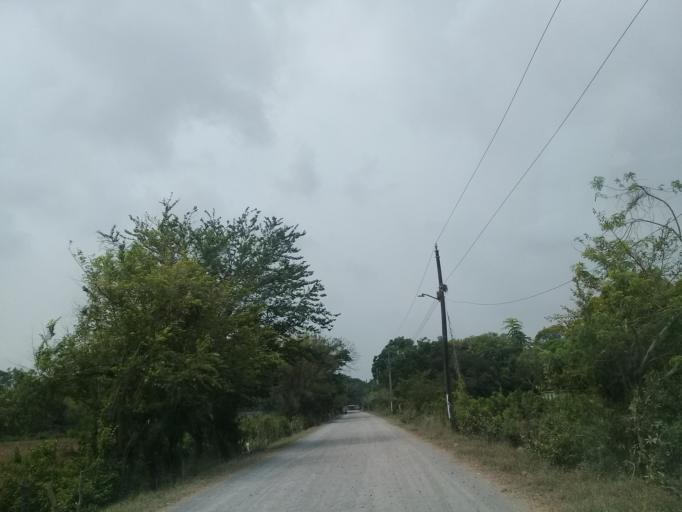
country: MX
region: Veracruz
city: El Tejar
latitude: 19.0569
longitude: -96.1983
